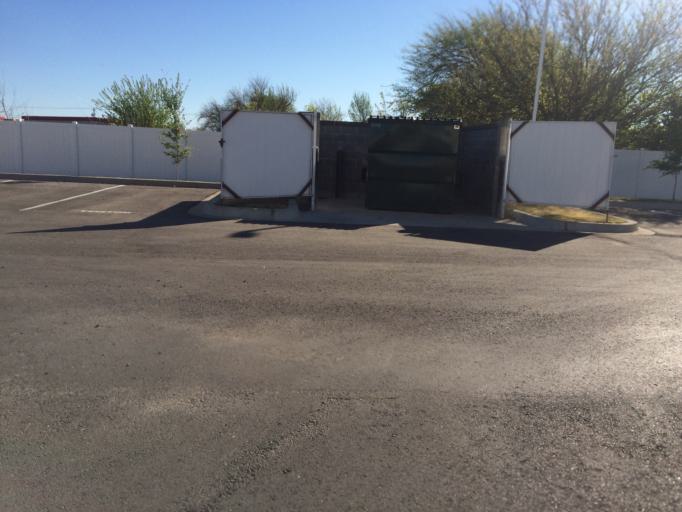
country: US
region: Oklahoma
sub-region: Cleveland County
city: Noble
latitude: 35.1776
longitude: -97.4168
